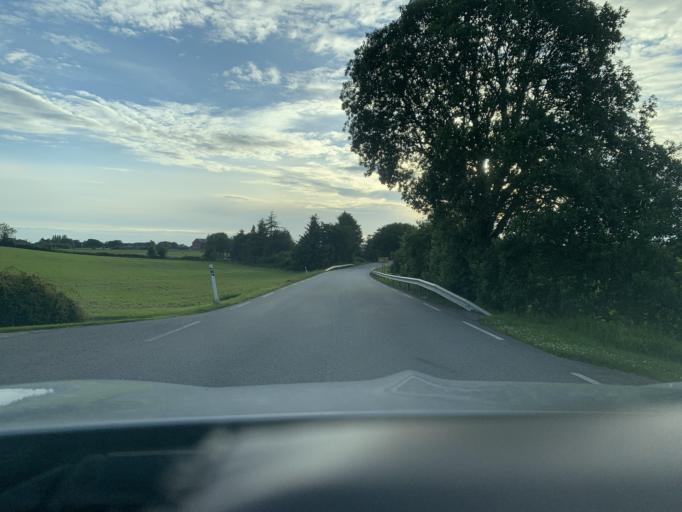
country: NO
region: Rogaland
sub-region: Time
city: Bryne
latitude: 58.7027
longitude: 5.7016
